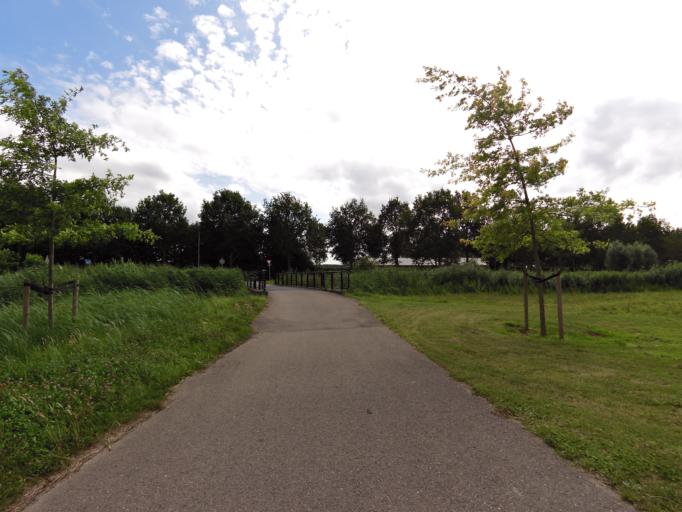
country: NL
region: South Holland
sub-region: Gemeente Sliedrecht
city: Sliedrecht
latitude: 51.7906
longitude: 4.7319
